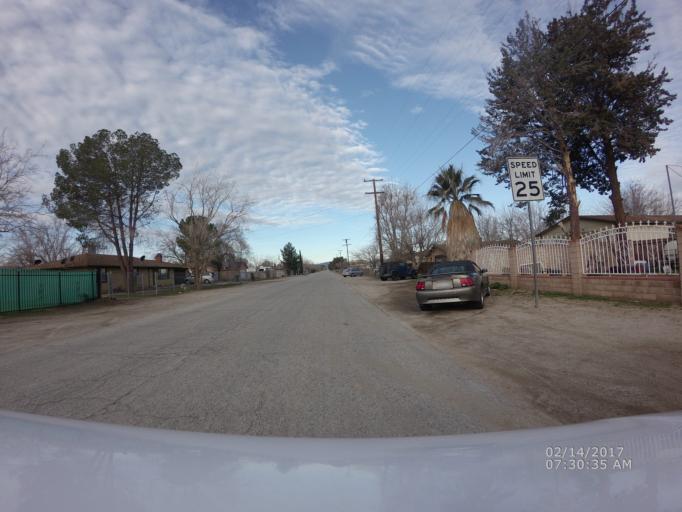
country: US
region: California
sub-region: Los Angeles County
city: Littlerock
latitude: 34.5448
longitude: -117.9409
